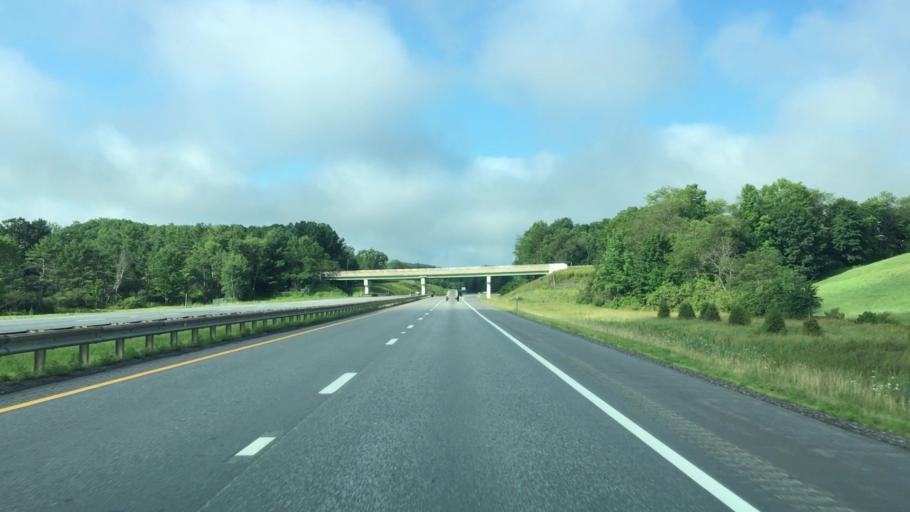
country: US
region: Maine
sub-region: Androscoggin County
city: Sabattus
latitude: 44.0849
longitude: -70.1103
